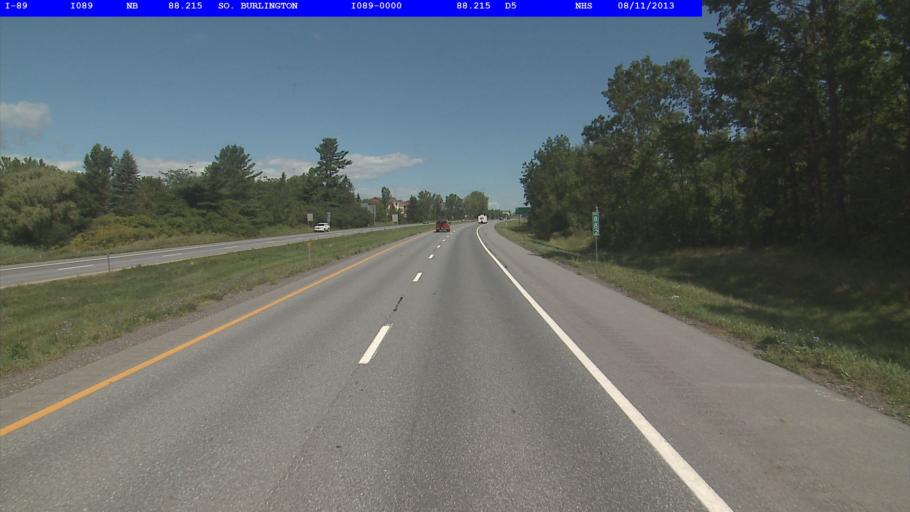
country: US
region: Vermont
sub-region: Chittenden County
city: South Burlington
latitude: 44.4626
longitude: -73.1853
